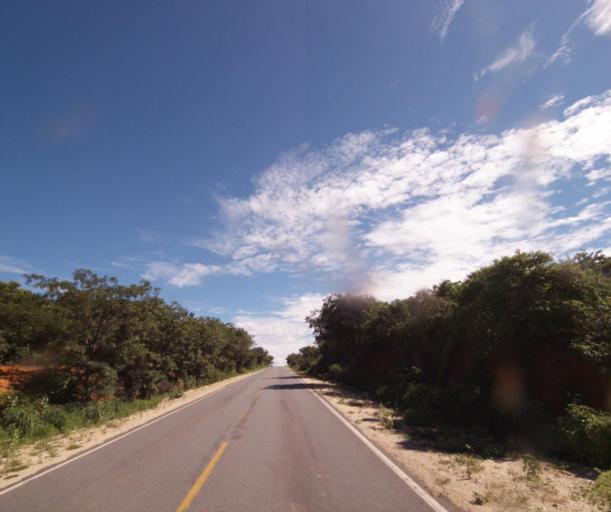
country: BR
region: Bahia
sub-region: Guanambi
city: Guanambi
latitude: -14.5674
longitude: -42.7027
